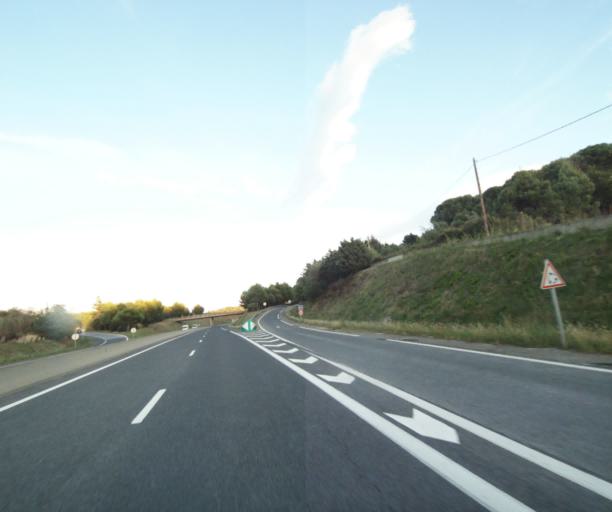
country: FR
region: Languedoc-Roussillon
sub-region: Departement des Pyrenees-Orientales
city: Collioure
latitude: 42.5313
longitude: 3.0522
